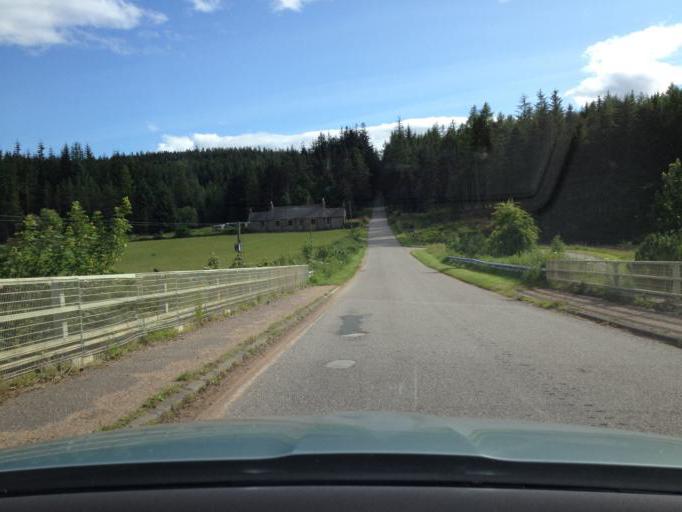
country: GB
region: Scotland
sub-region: Aberdeenshire
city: Banchory
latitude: 56.9644
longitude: -2.5751
